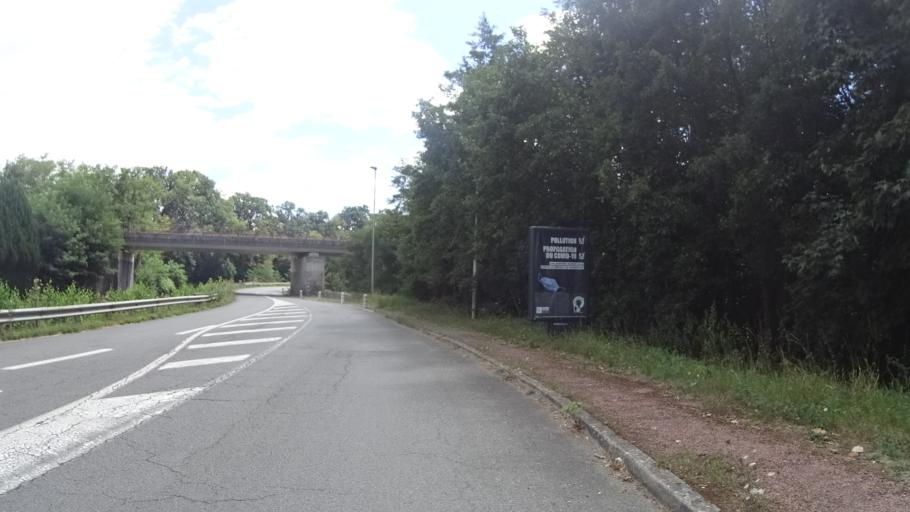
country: FR
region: Bourgogne
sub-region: Departement de Saone-et-Loire
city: Saint-Vallier
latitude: 46.6473
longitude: 4.3355
